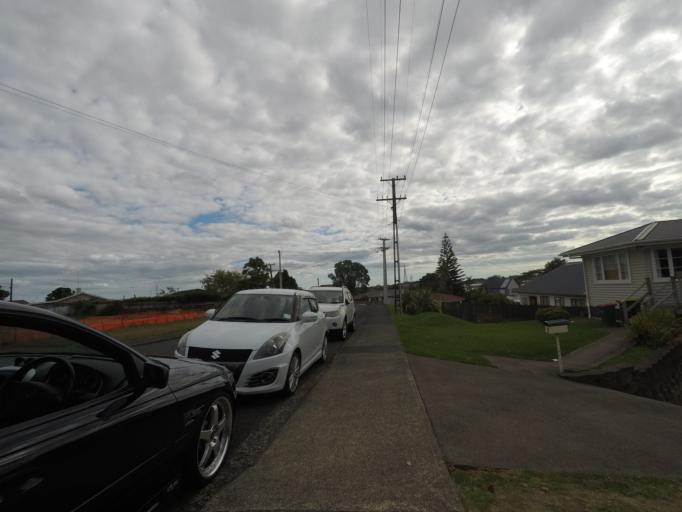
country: NZ
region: Auckland
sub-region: Auckland
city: Papakura
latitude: -37.0583
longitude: 174.9321
